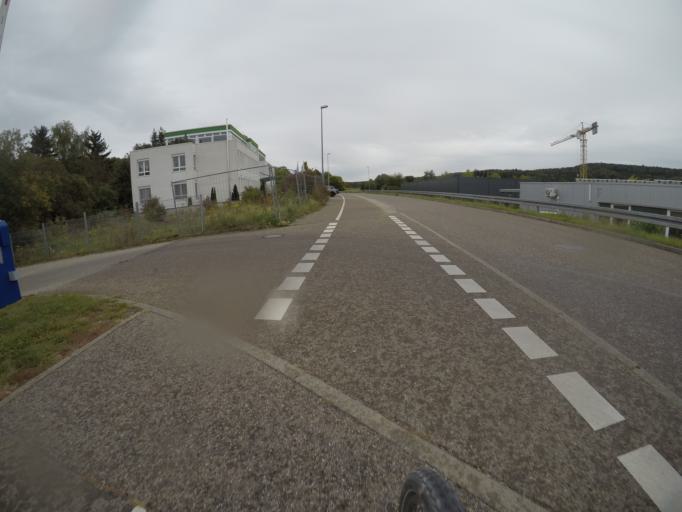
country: DE
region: Baden-Wuerttemberg
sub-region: Regierungsbezirk Stuttgart
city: Leonberg
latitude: 48.7836
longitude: 9.0206
